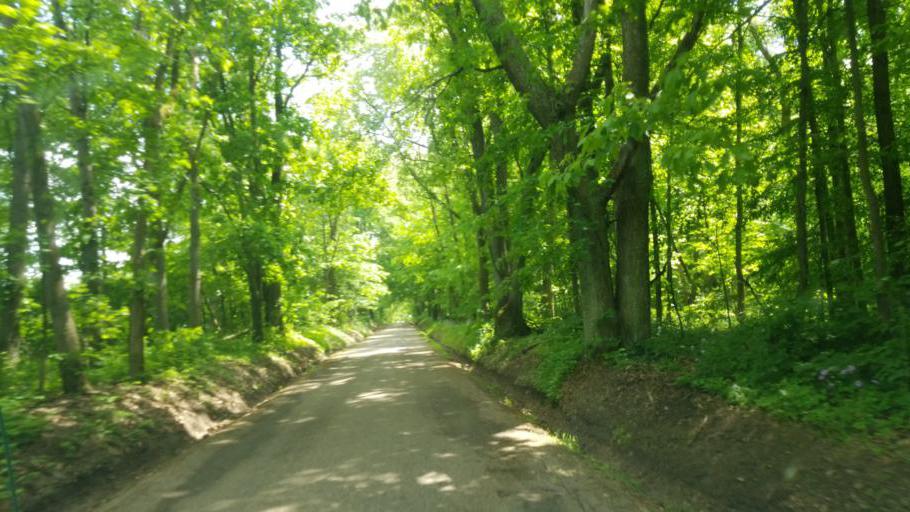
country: US
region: Ohio
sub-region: Ashland County
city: Loudonville
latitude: 40.6748
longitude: -82.3488
